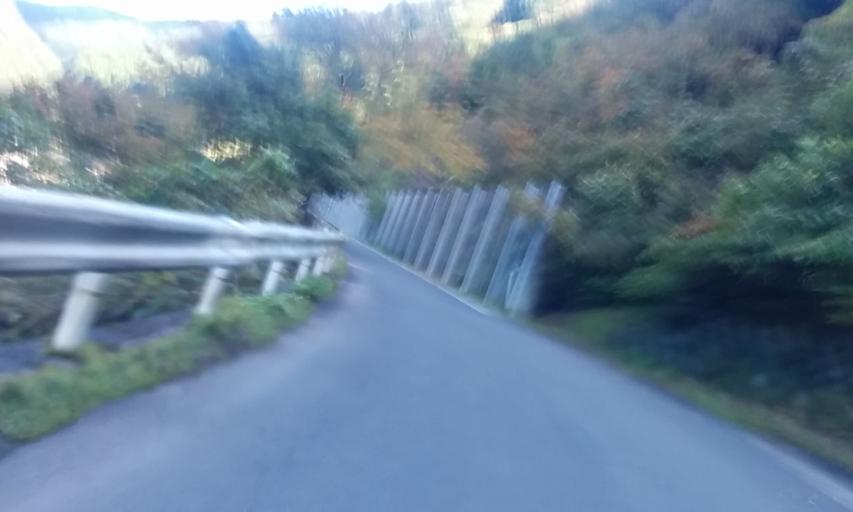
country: JP
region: Kyoto
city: Kameoka
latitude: 35.1271
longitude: 135.5677
